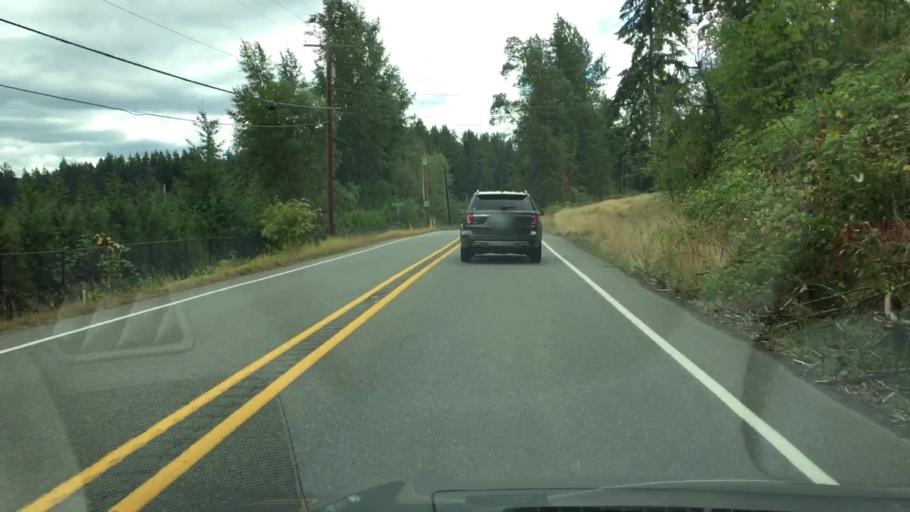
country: US
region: Washington
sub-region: Pierce County
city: Eatonville
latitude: 46.9305
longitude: -122.2817
